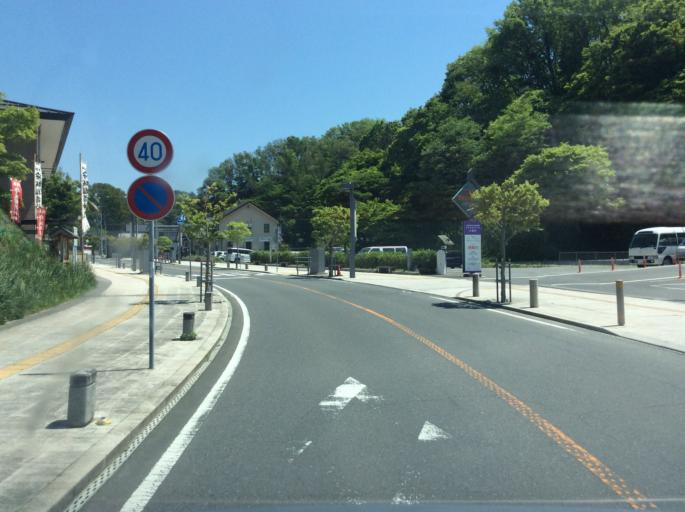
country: JP
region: Fukushima
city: Miharu
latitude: 37.4410
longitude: 140.4929
